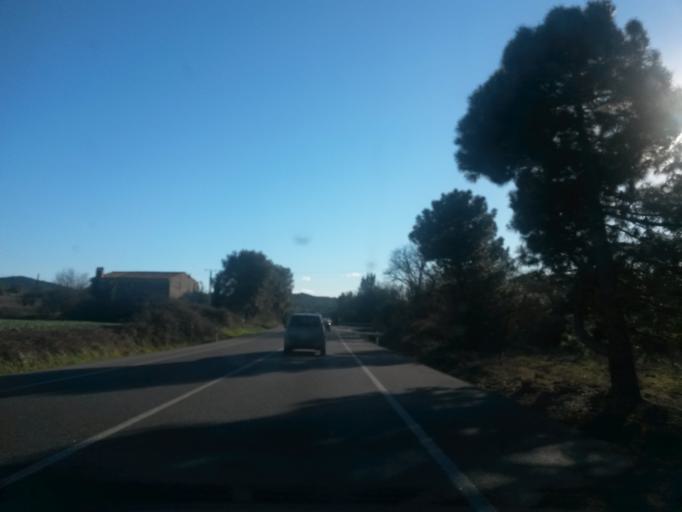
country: ES
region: Catalonia
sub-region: Provincia de Girona
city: Vidreres
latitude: 41.7671
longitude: 2.7586
